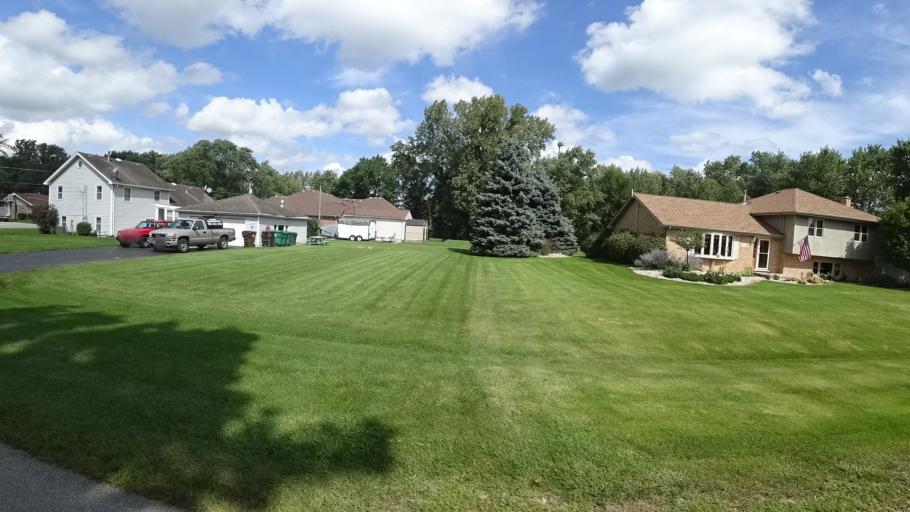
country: US
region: Illinois
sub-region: Cook County
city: Tinley Park
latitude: 41.5661
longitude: -87.7713
